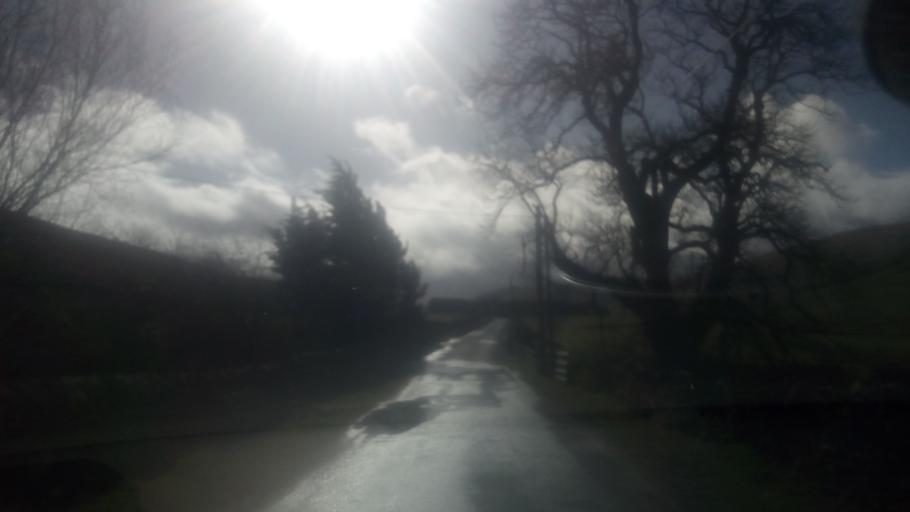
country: GB
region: Scotland
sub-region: The Scottish Borders
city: Innerleithen
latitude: 55.5048
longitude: -3.1104
